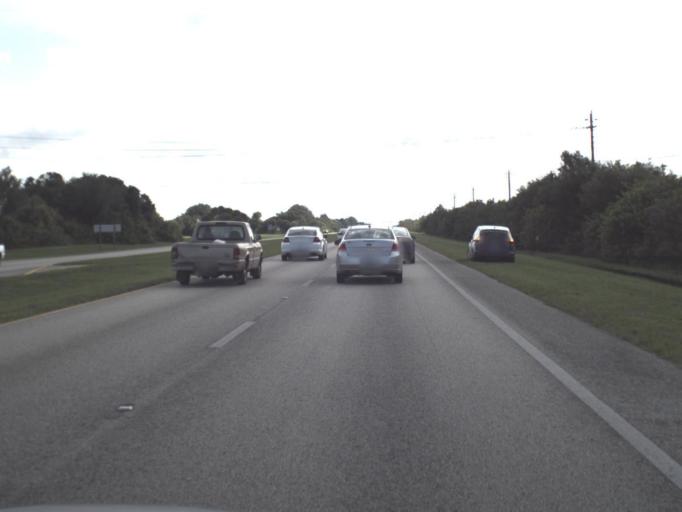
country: US
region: Florida
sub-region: Sarasota County
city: Plantation
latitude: 27.0496
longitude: -82.3859
